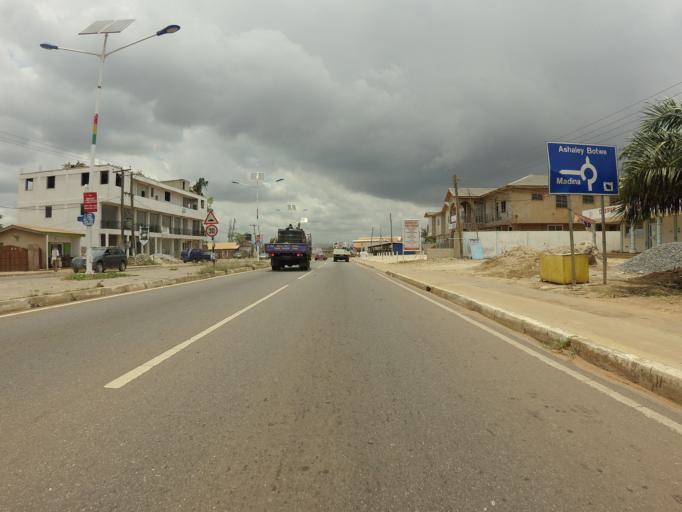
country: GH
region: Greater Accra
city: Medina Estates
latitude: 5.6735
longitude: -0.1515
